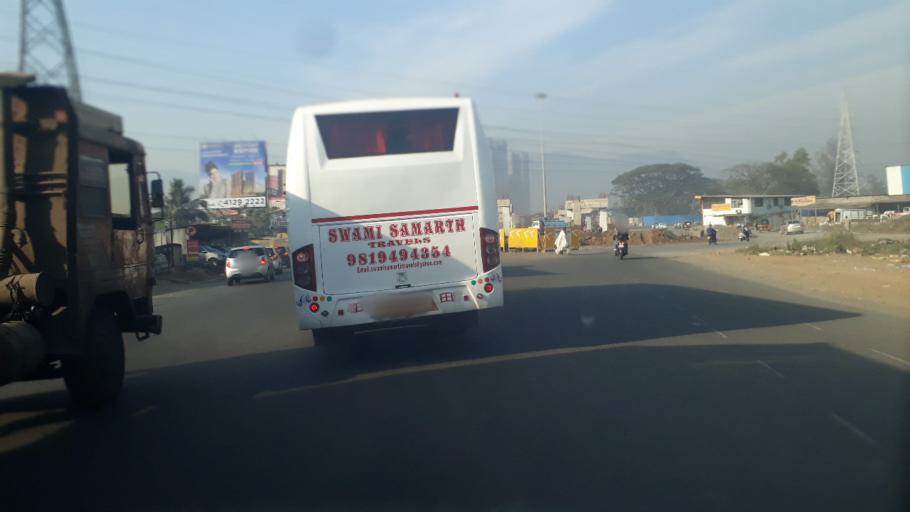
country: IN
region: Maharashtra
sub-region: Raigarh
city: Kalundri
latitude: 18.9686
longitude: 73.1335
